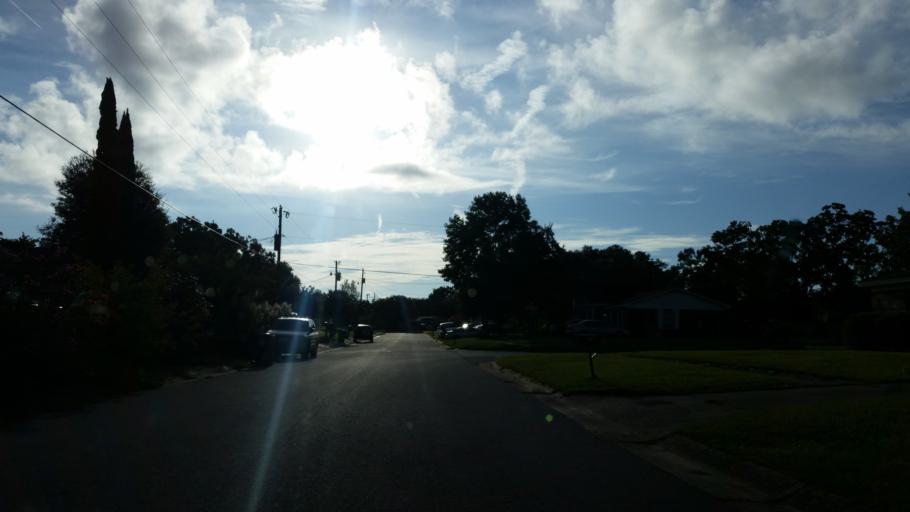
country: US
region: Florida
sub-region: Escambia County
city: Bellview
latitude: 30.4456
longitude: -87.3097
